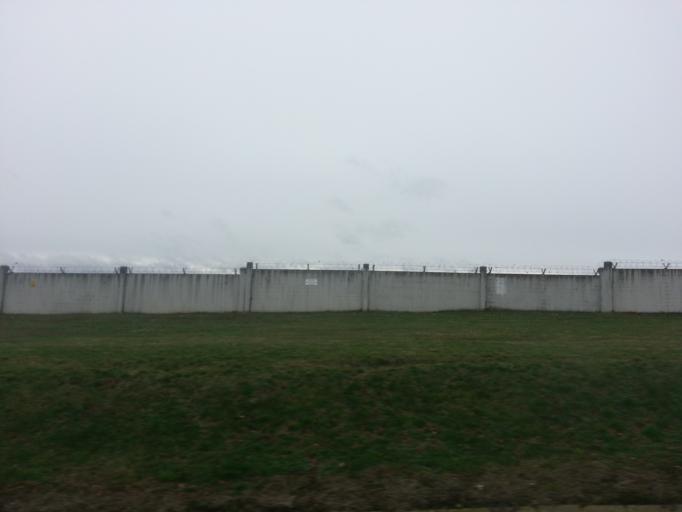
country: CZ
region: Central Bohemia
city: Tuchomerice
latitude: 50.1081
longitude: 14.2860
